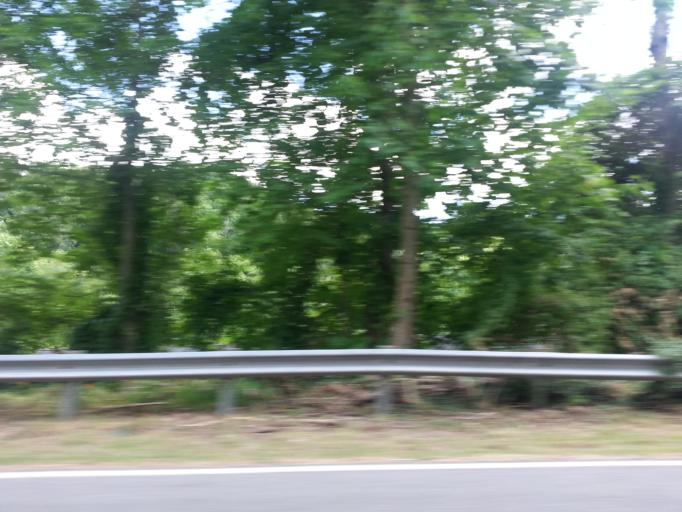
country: US
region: Kentucky
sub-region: Harlan County
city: Harlan
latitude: 36.8882
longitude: -83.2833
